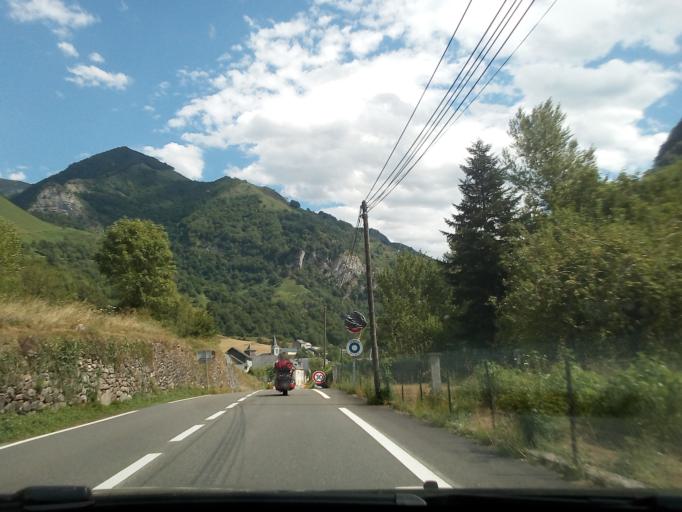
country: FR
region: Aquitaine
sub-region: Departement des Pyrenees-Atlantiques
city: Laruns
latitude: 42.9377
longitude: -0.5920
